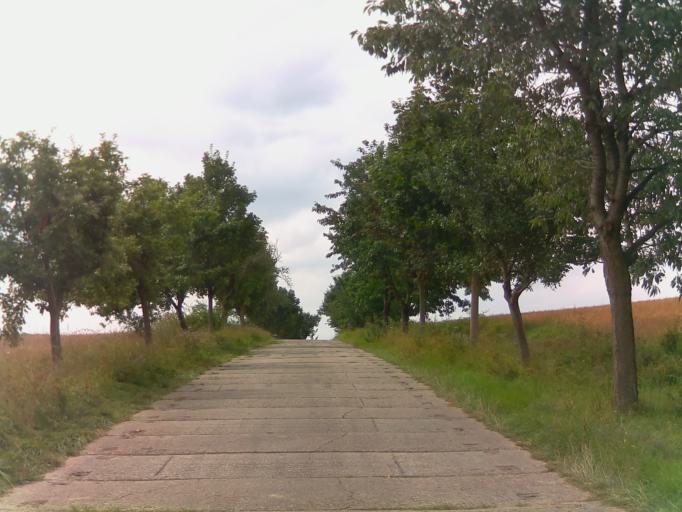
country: DE
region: Thuringia
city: Rittersdorf
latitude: 50.7659
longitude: 11.2762
